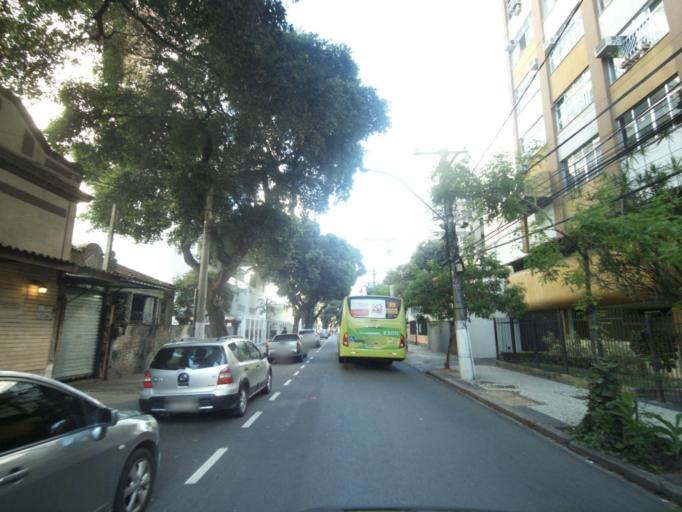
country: BR
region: Rio de Janeiro
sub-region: Niteroi
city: Niteroi
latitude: -22.9005
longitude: -43.1030
